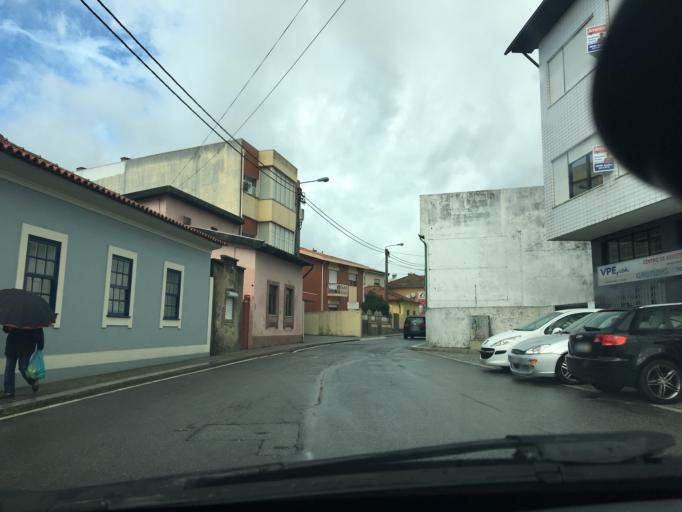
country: PT
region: Porto
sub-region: Matosinhos
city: Santa Cruz do Bispo
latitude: 41.2393
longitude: -8.6646
